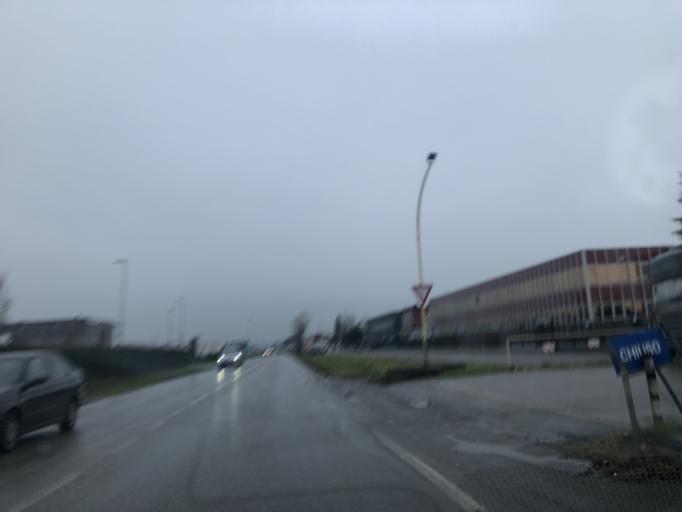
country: IT
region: Emilia-Romagna
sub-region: Provincia di Modena
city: Modena
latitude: 44.6566
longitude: 10.8818
